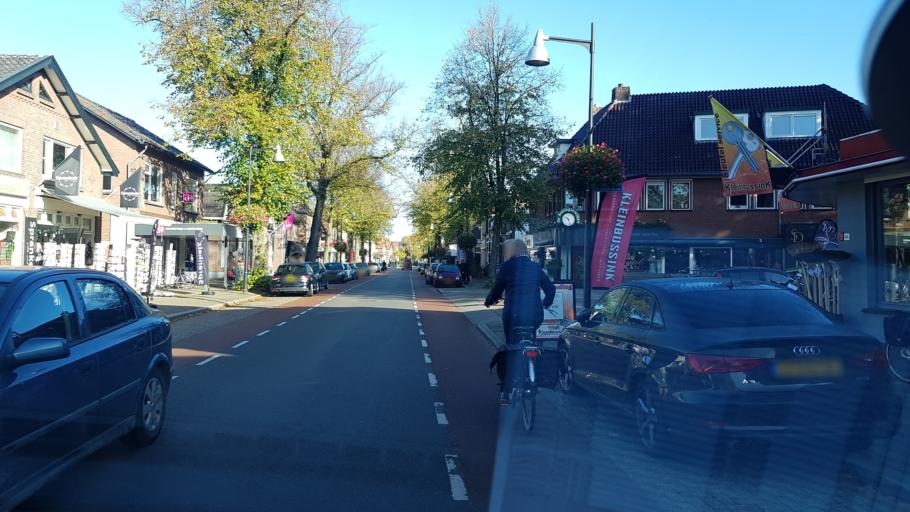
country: NL
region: Gelderland
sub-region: Gemeente Apeldoorn
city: Apeldoorn
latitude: 52.2258
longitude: 5.9570
